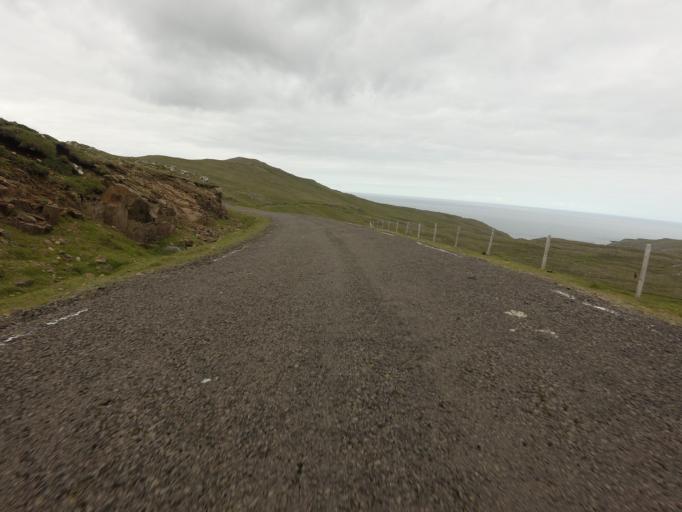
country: FO
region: Suduroy
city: Vagur
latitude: 61.4331
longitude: -6.7561
